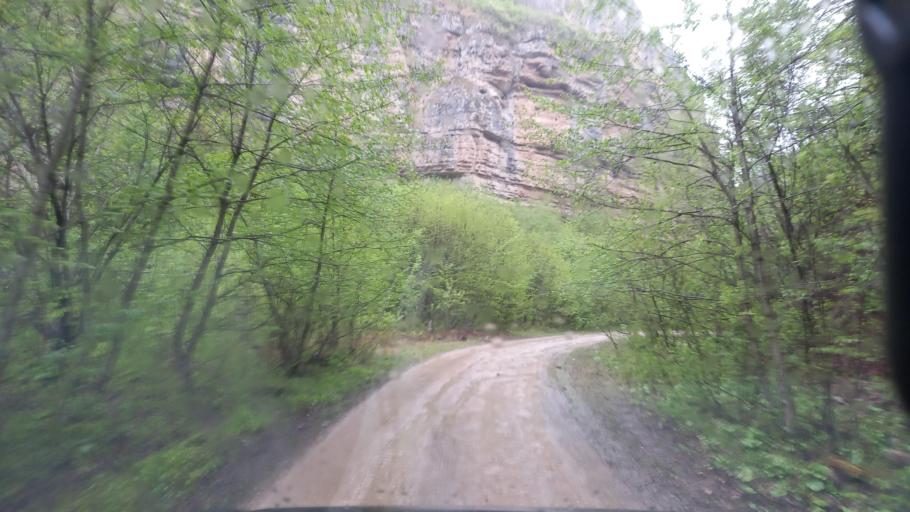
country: RU
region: Kabardino-Balkariya
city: Bylym
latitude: 43.5874
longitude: 43.0165
